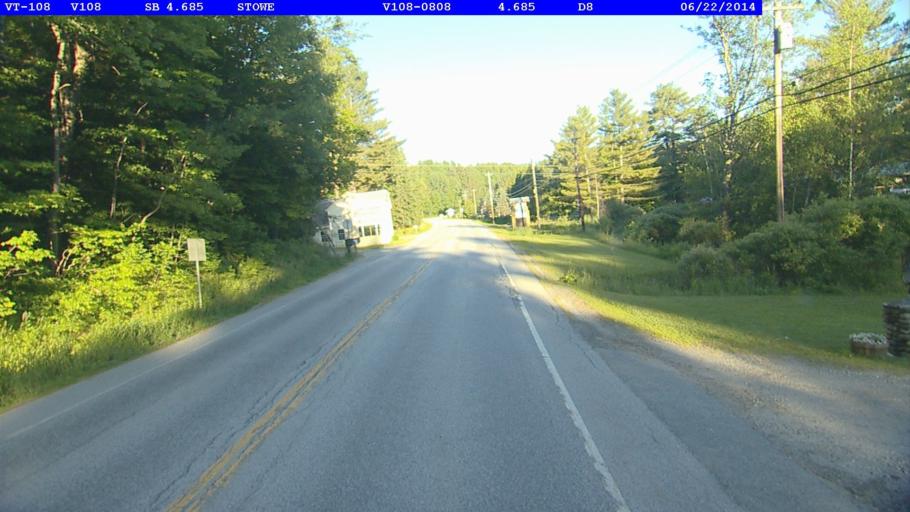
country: US
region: Vermont
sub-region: Lamoille County
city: Morristown
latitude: 44.5006
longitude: -72.7483
